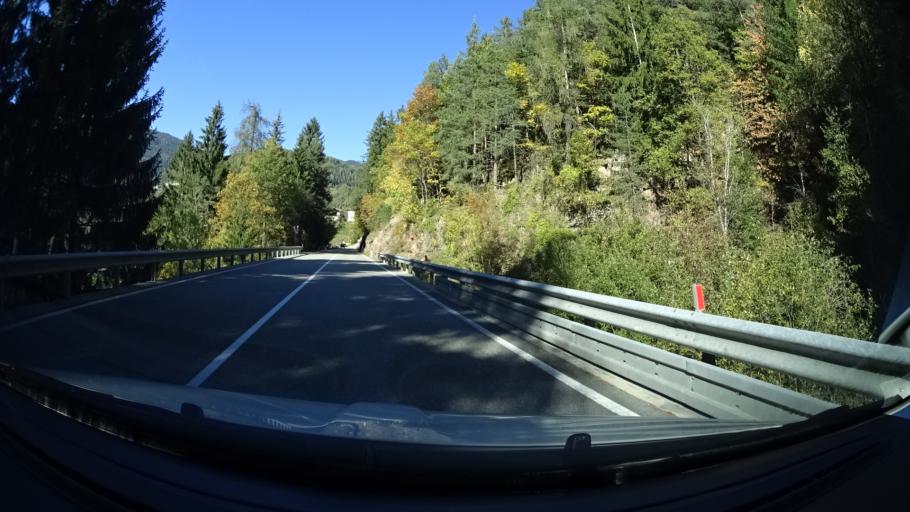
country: IT
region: Trentino-Alto Adige
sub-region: Provincia di Trento
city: Valfloriana
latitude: 46.2583
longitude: 11.3558
